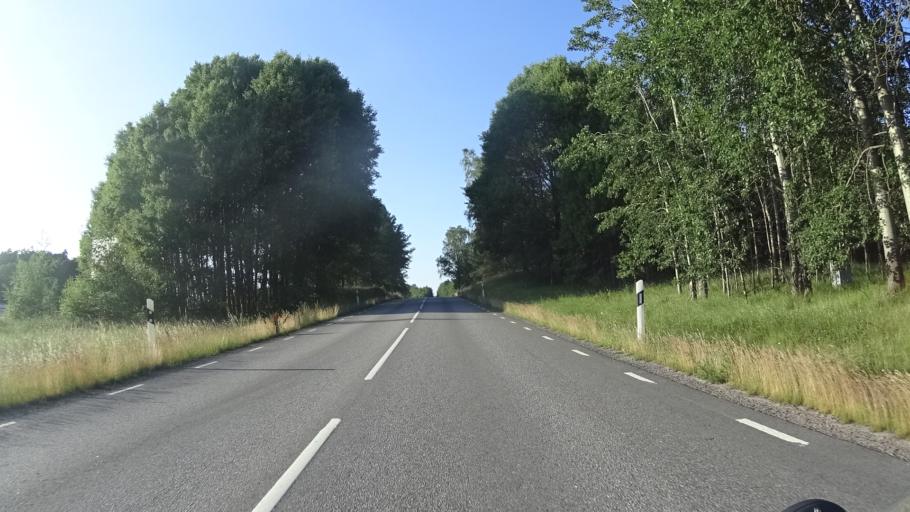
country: SE
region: Stockholm
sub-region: Sodertalje Kommun
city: Pershagen
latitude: 59.1427
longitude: 17.6506
